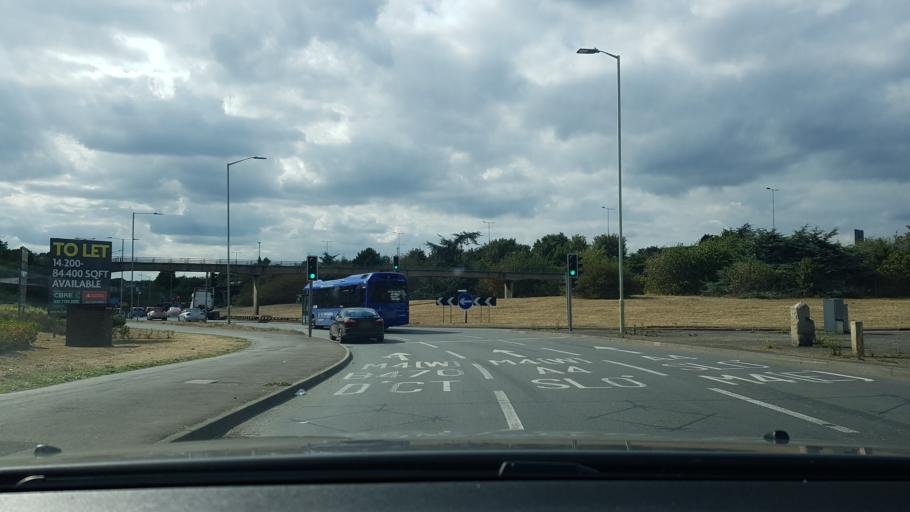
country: GB
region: England
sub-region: Royal Borough of Windsor and Maidenhead
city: Horton
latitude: 51.4910
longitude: -0.5409
